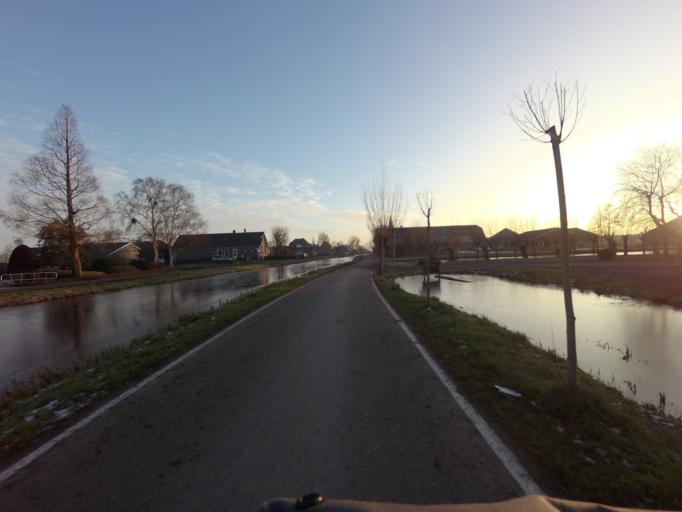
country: NL
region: Utrecht
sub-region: Gemeente Woerden
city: Woerden
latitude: 52.1280
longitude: 4.8938
